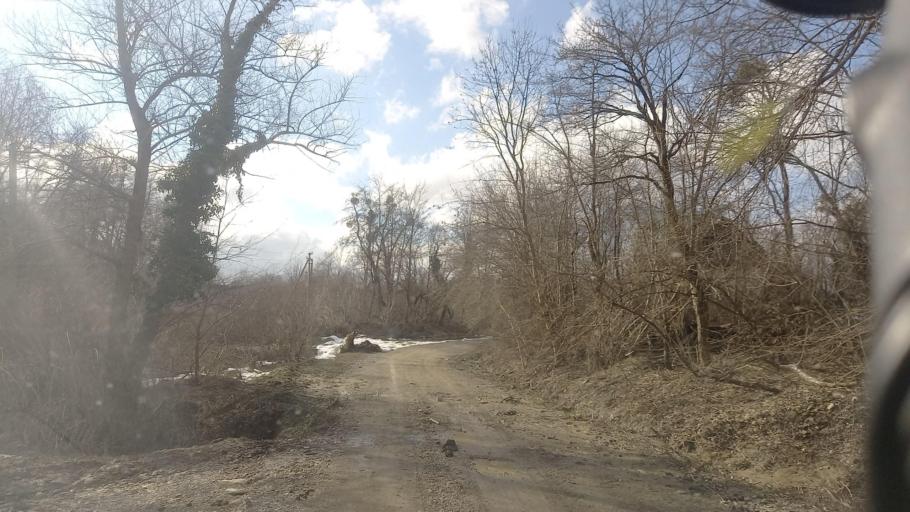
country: RU
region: Krasnodarskiy
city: Smolenskaya
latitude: 44.6015
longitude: 38.8709
